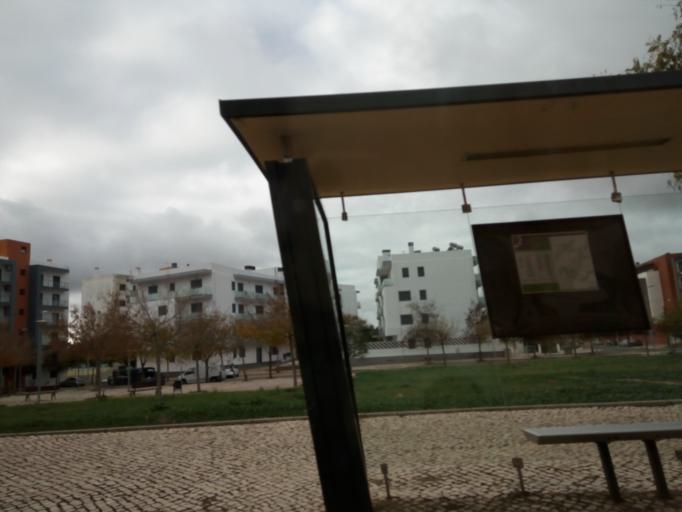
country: PT
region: Faro
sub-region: Loule
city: Loule
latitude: 37.1328
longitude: -8.0085
